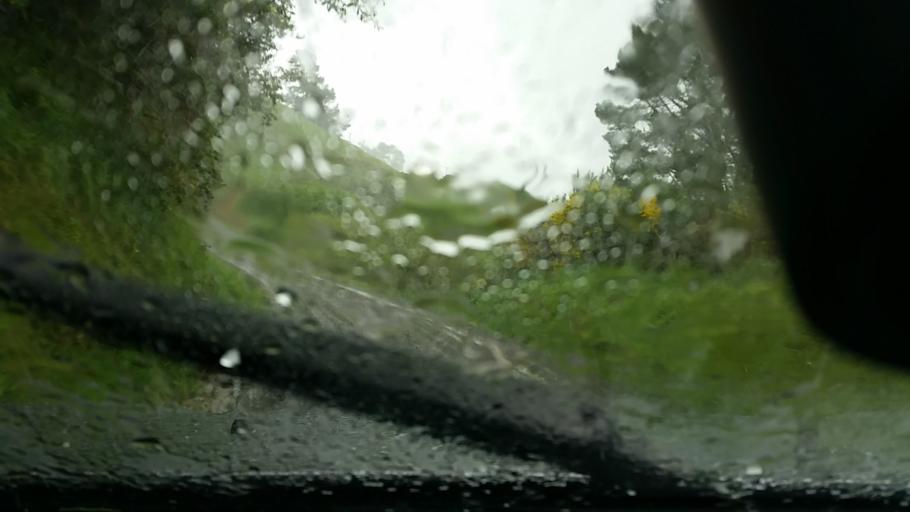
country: NZ
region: Waikato
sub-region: Taupo District
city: Taupo
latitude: -38.4786
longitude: 176.2169
